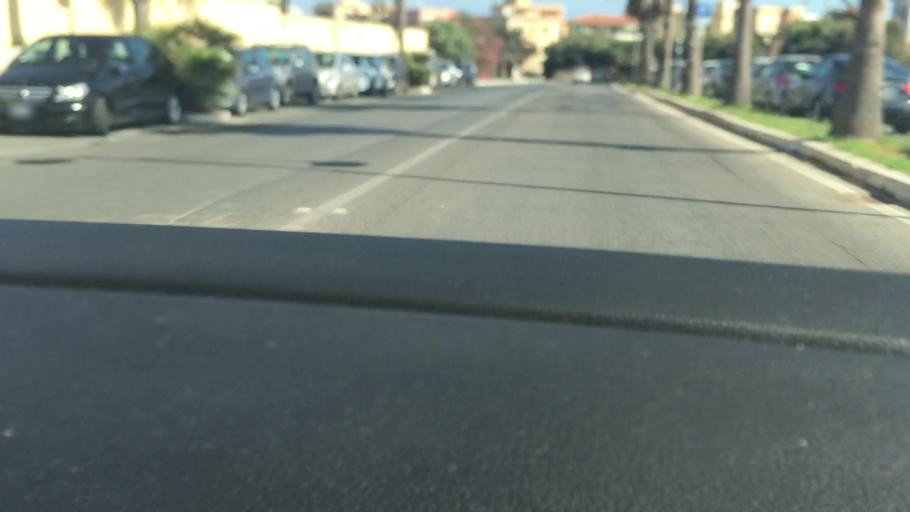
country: IT
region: Latium
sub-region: Citta metropolitana di Roma Capitale
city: Anzio
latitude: 41.4468
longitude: 12.6209
